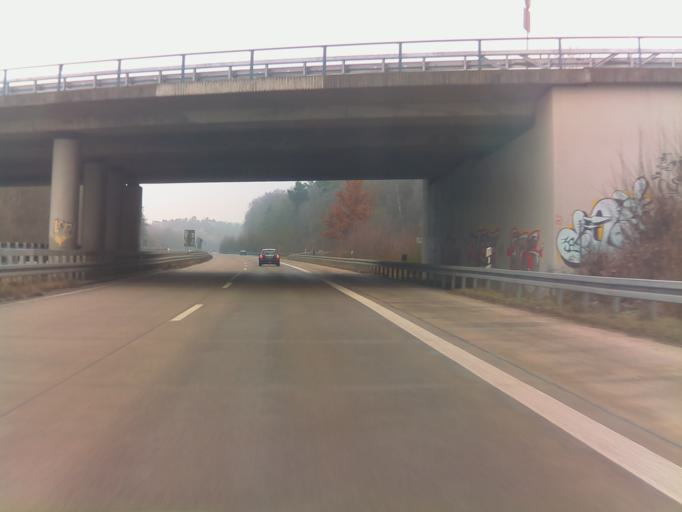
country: DE
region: Hesse
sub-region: Regierungsbezirk Darmstadt
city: Munster
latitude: 49.9069
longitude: 8.8693
